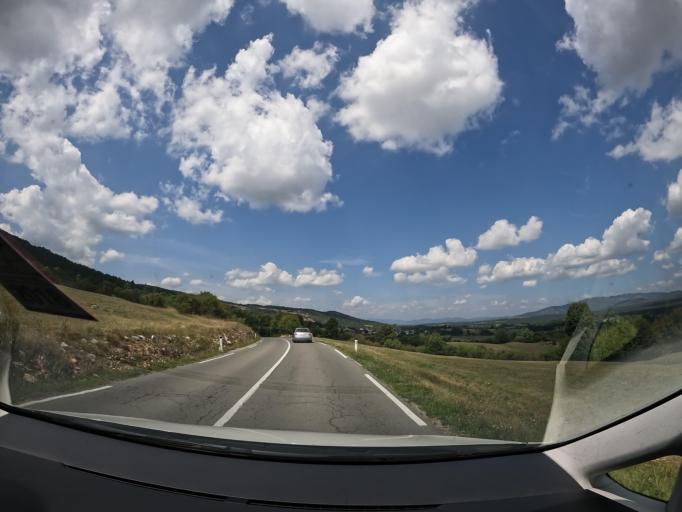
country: SI
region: Pivka
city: Pivka
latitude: 45.6300
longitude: 14.2306
